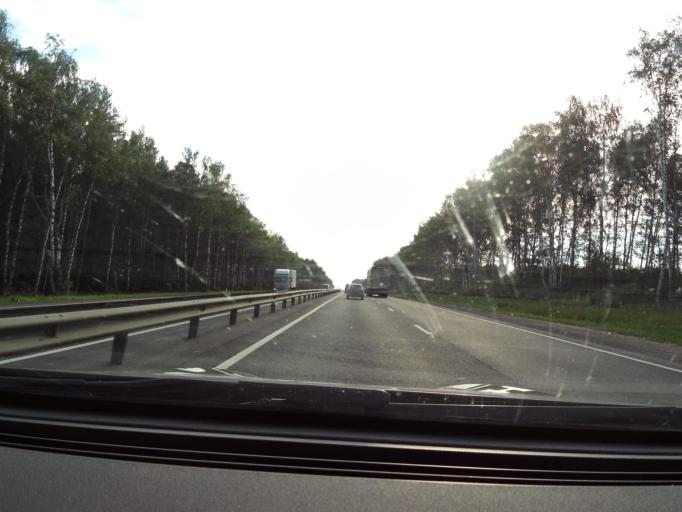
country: RU
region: Vladimir
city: Kameshkovo
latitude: 56.1967
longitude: 40.9997
